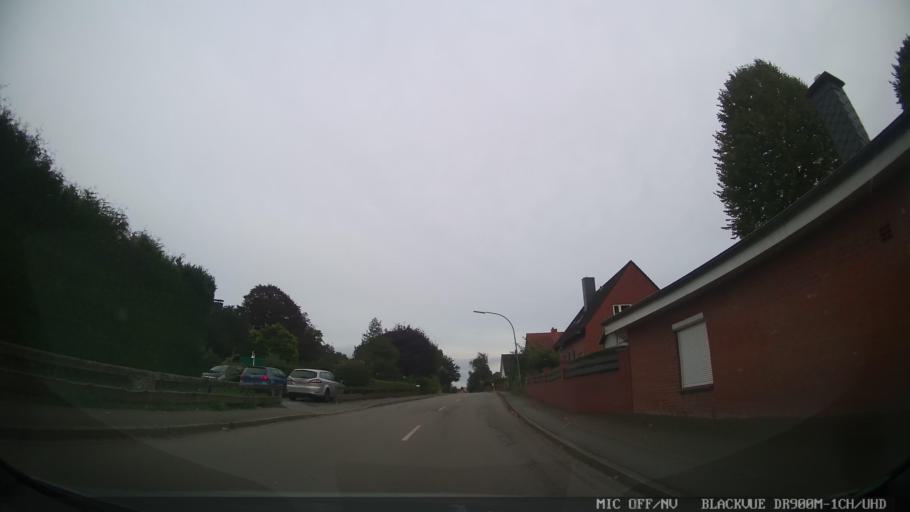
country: DE
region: Schleswig-Holstein
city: Grube
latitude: 54.2738
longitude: 11.0571
